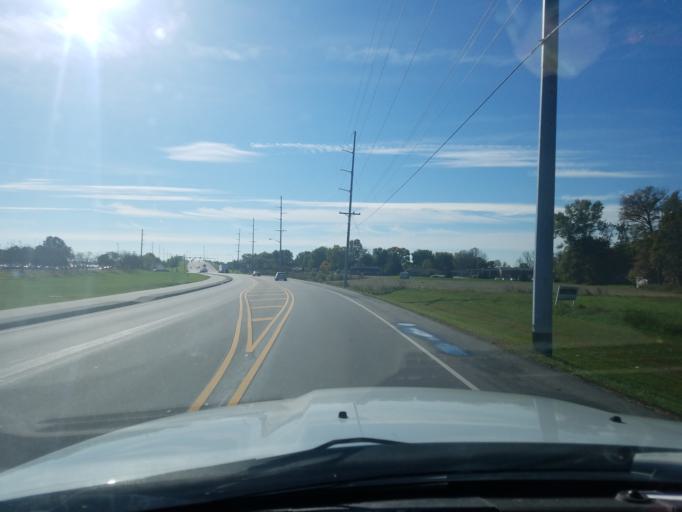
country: US
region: Indiana
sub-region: Jackson County
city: Seymour
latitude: 38.9679
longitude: -85.8710
